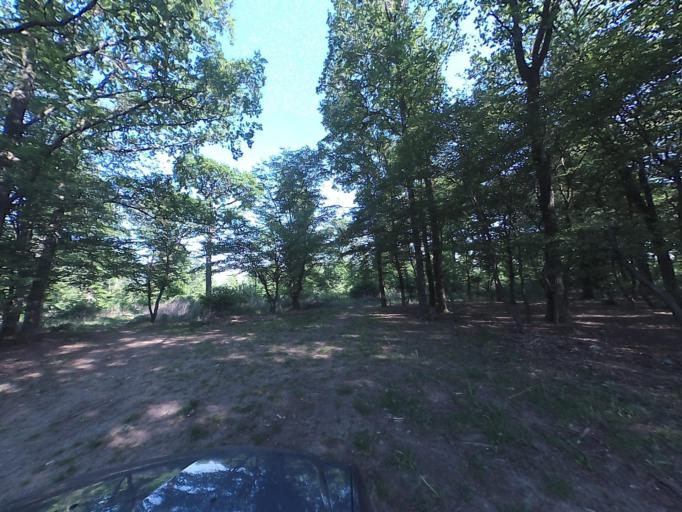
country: RO
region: Neamt
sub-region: Comuna Dulcesti
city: Dulcesti
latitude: 46.9965
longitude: 26.7836
